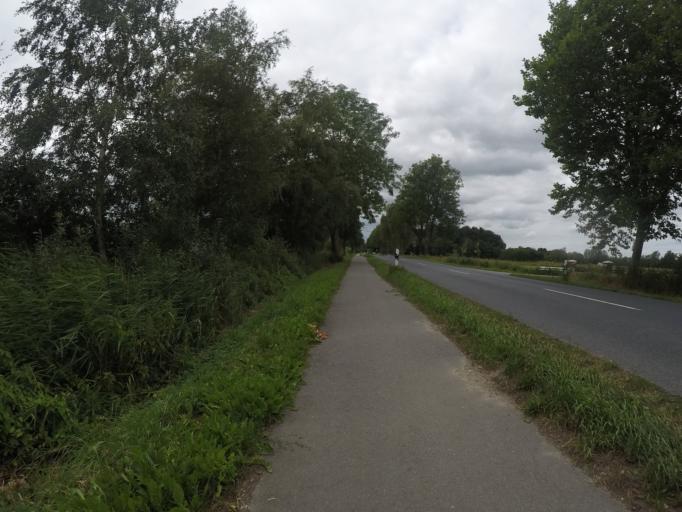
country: DE
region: Lower Saxony
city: Grossenworden
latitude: 53.6734
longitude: 9.2839
